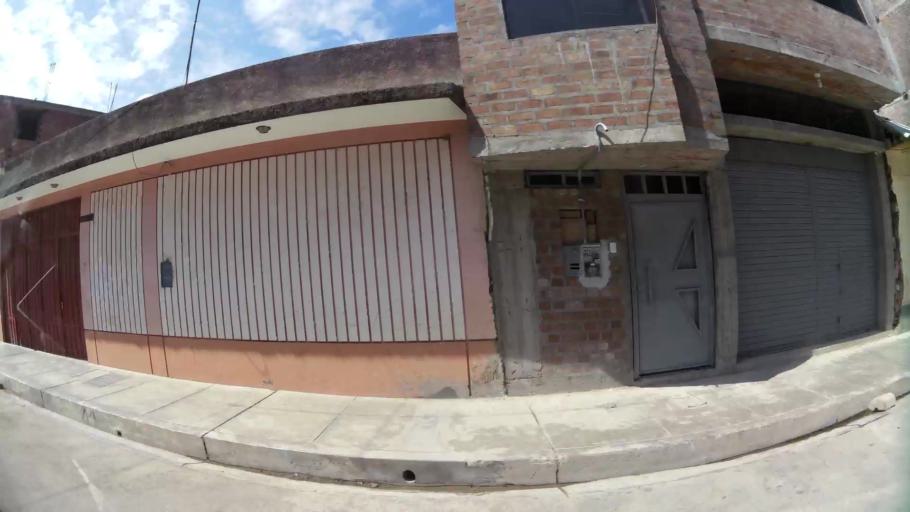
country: PE
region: Junin
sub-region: Provincia de Huancayo
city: El Tambo
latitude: -12.0750
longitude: -75.2155
